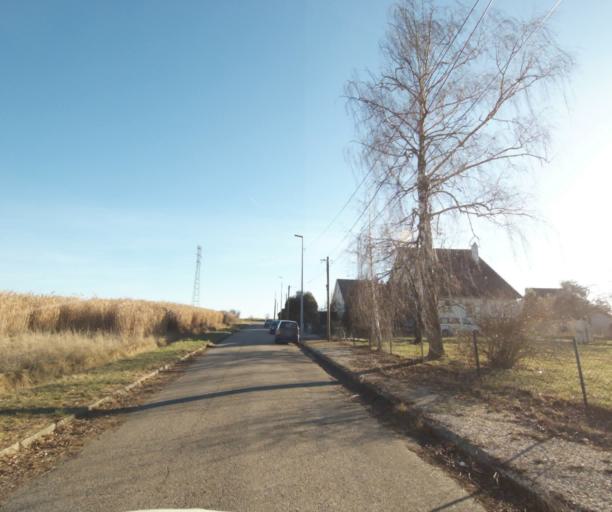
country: FR
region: Lorraine
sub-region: Departement de Meurthe-et-Moselle
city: Art-sur-Meurthe
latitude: 48.6360
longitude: 6.2705
